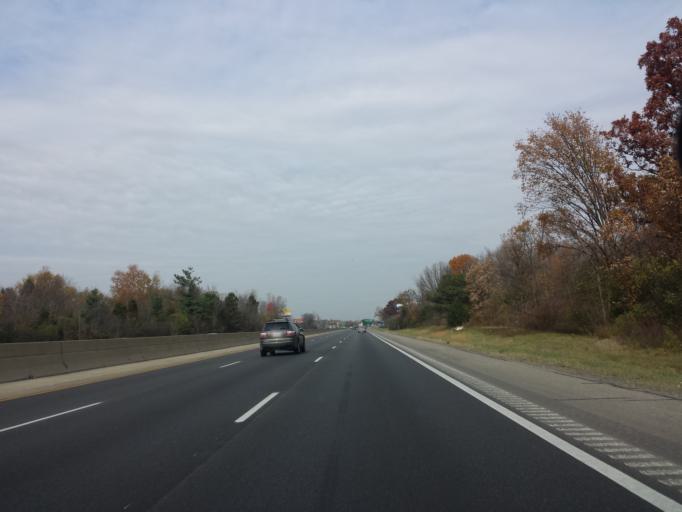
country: US
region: Michigan
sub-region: Genesee County
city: Beecher
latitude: 43.0507
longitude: -83.7576
